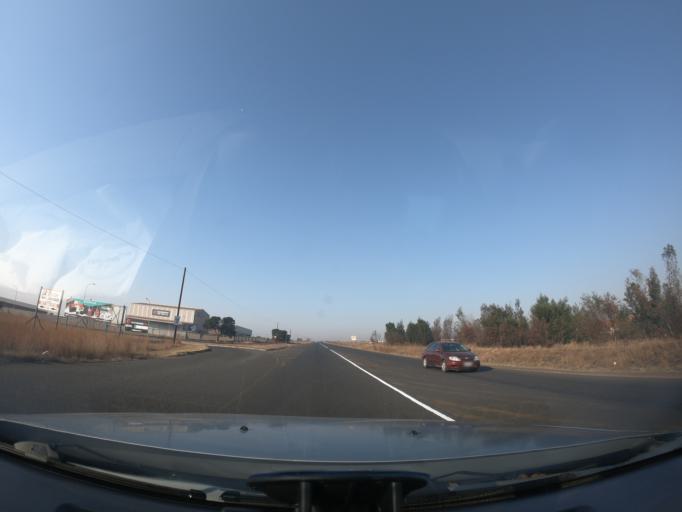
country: ZA
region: Mpumalanga
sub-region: Nkangala District Municipality
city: Middelburg
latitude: -25.8174
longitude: 29.4614
